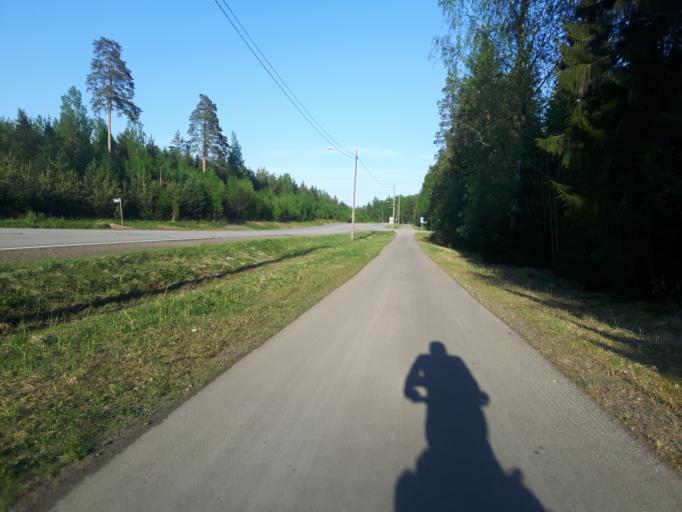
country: FI
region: Uusimaa
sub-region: Loviisa
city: Lovisa
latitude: 60.4551
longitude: 26.1608
